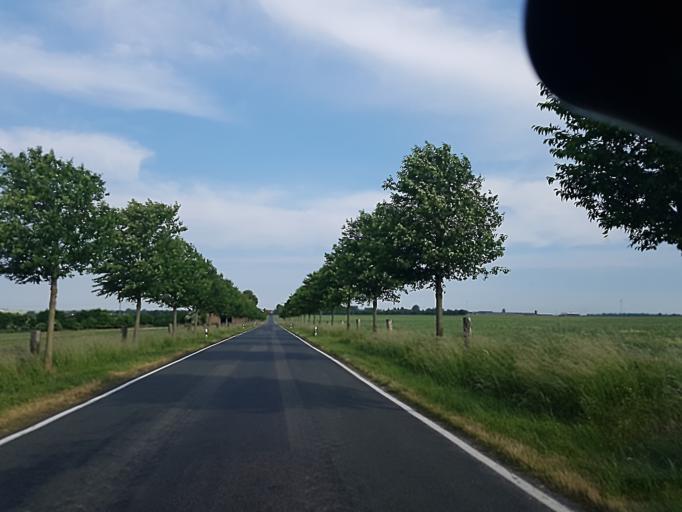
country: DE
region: Saxony-Anhalt
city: Kropstadt
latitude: 51.9929
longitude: 12.7902
